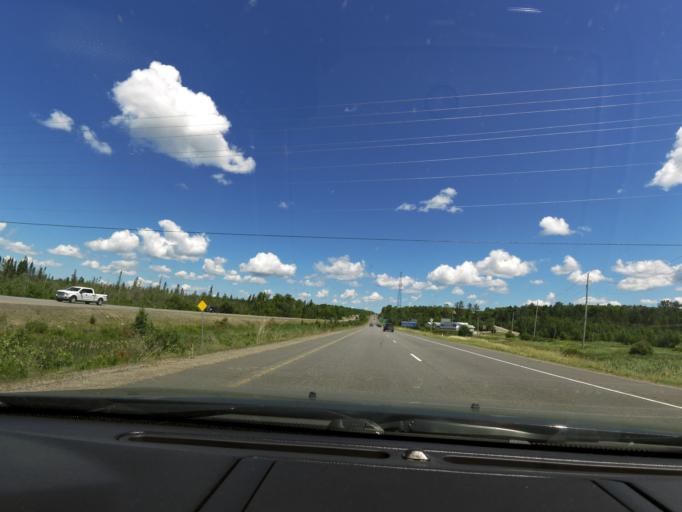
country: CA
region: Ontario
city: Bracebridge
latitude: 45.1964
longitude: -79.3135
